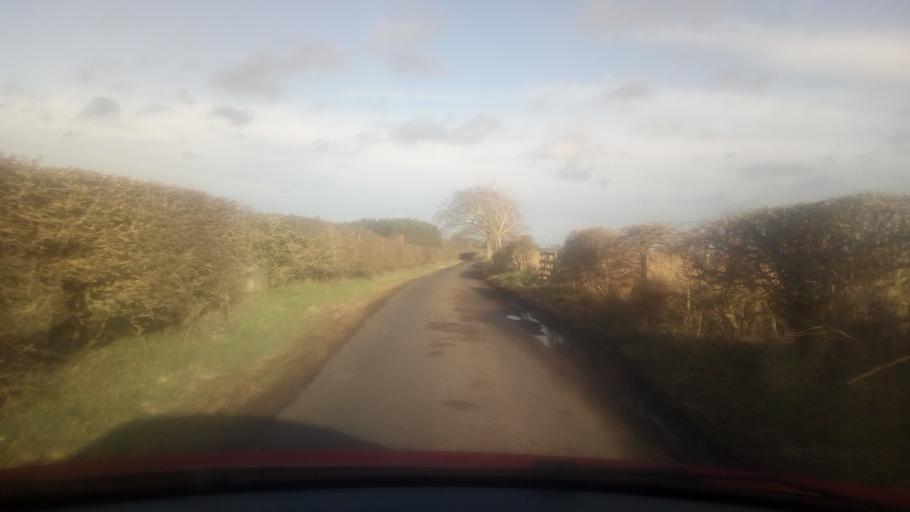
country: GB
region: Scotland
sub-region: The Scottish Borders
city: Duns
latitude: 55.7370
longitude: -2.3461
